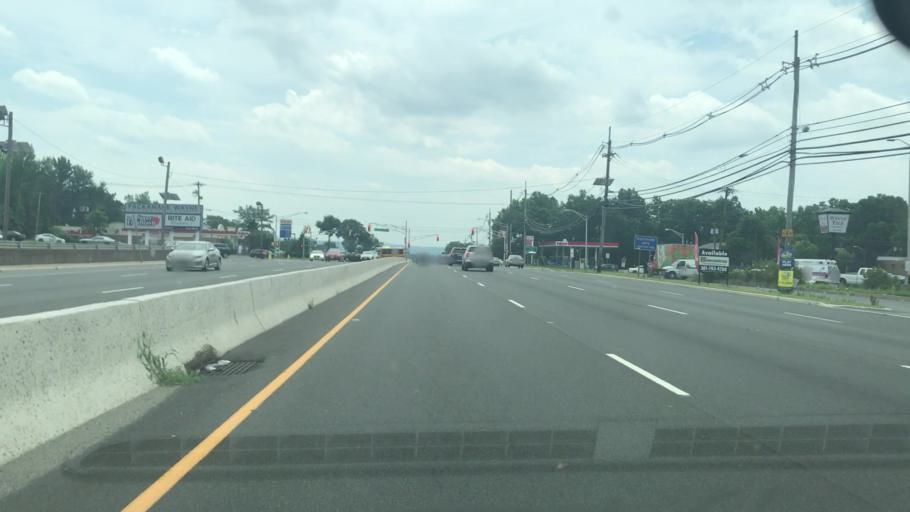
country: US
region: New Jersey
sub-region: Passaic County
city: Wayne
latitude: 40.9345
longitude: -74.2692
